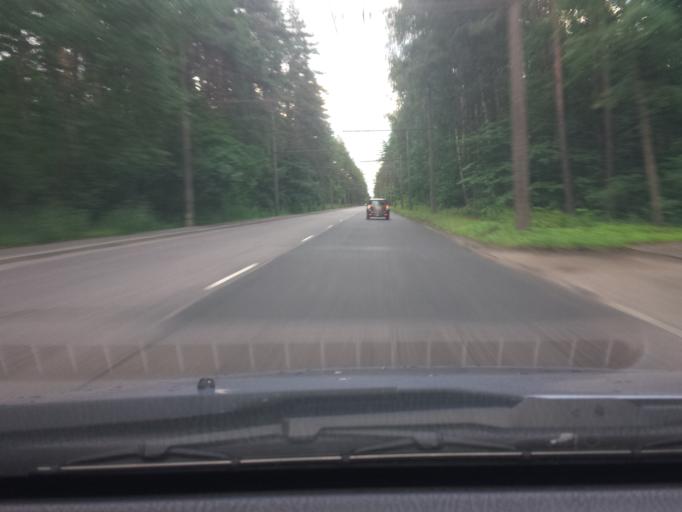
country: LV
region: Stopini
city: Ulbroka
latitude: 56.9645
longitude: 24.2116
